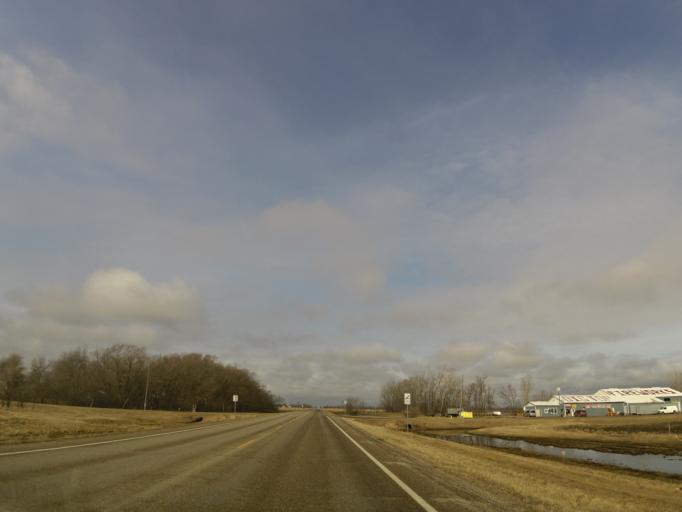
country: US
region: North Dakota
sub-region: Traill County
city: Hillsboro
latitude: 47.4979
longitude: -97.0906
